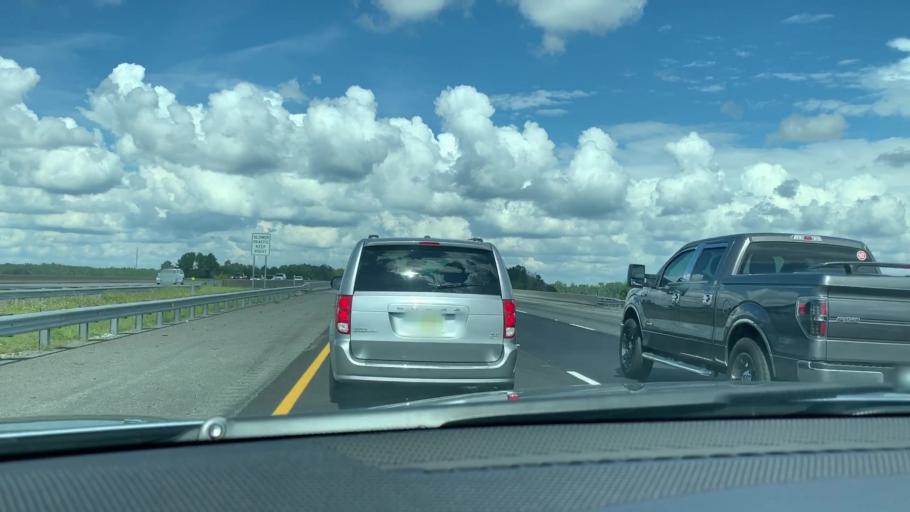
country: US
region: Georgia
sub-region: Camden County
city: Woodbine
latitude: 31.0355
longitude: -81.6537
